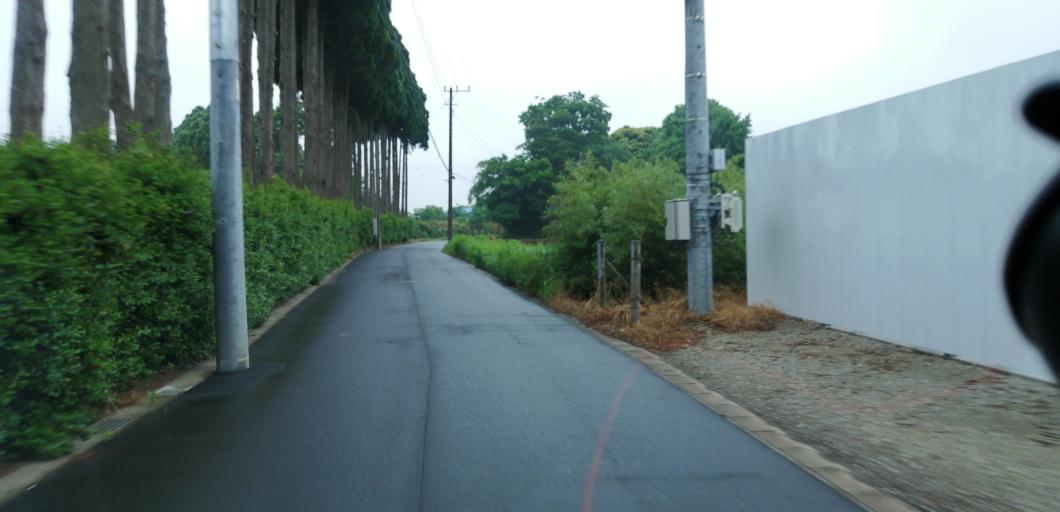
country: JP
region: Chiba
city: Yachimata
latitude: 35.5847
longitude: 140.2691
